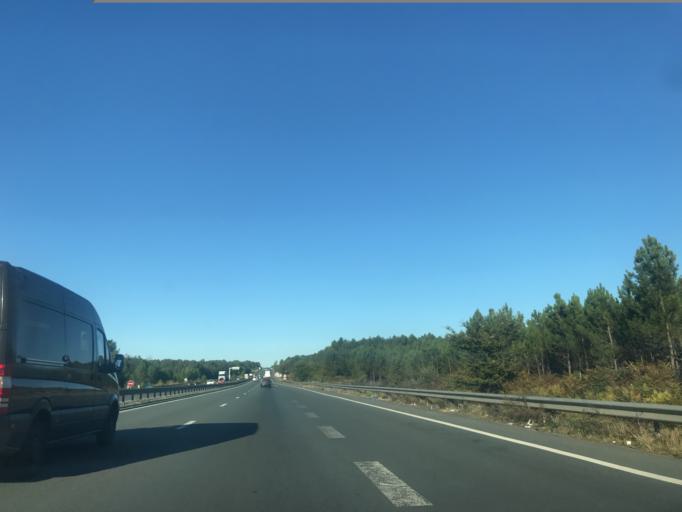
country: FR
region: Aquitaine
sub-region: Departement de la Gironde
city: Laruscade
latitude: 45.1729
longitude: -0.3324
